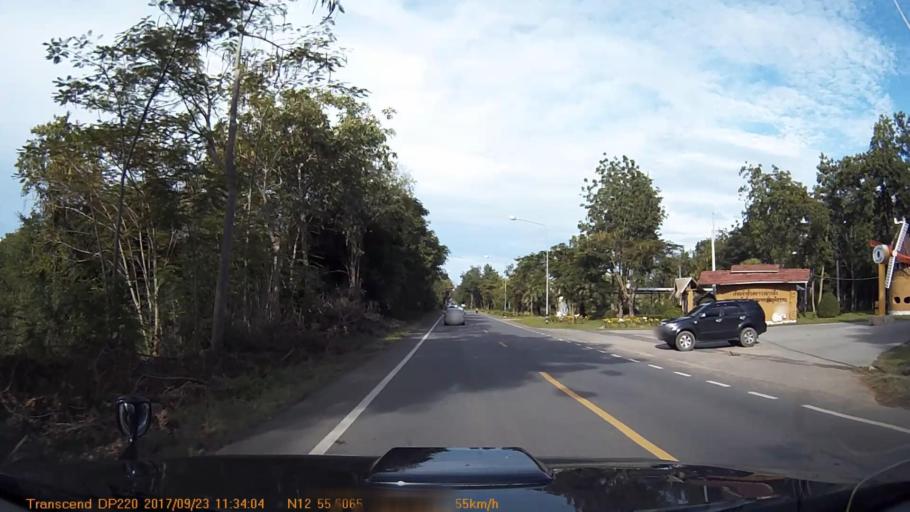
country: TH
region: Phetchaburi
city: Kaeng Krachan
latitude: 12.9268
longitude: 99.7312
